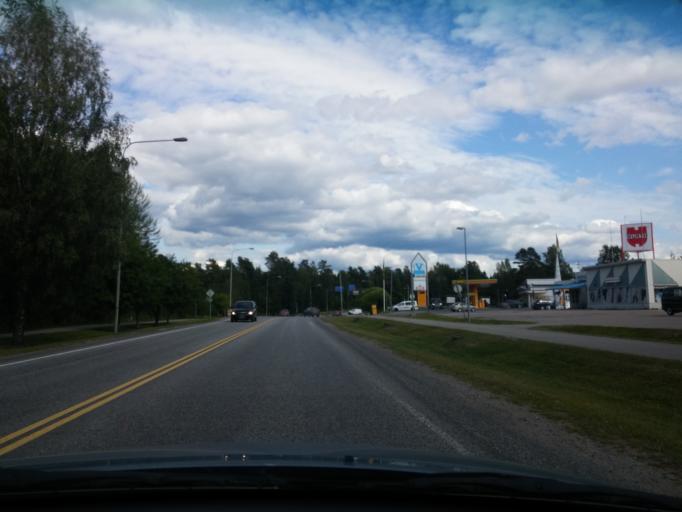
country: FI
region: Central Finland
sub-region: Keuruu
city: Keuruu
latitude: 62.2546
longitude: 24.7170
